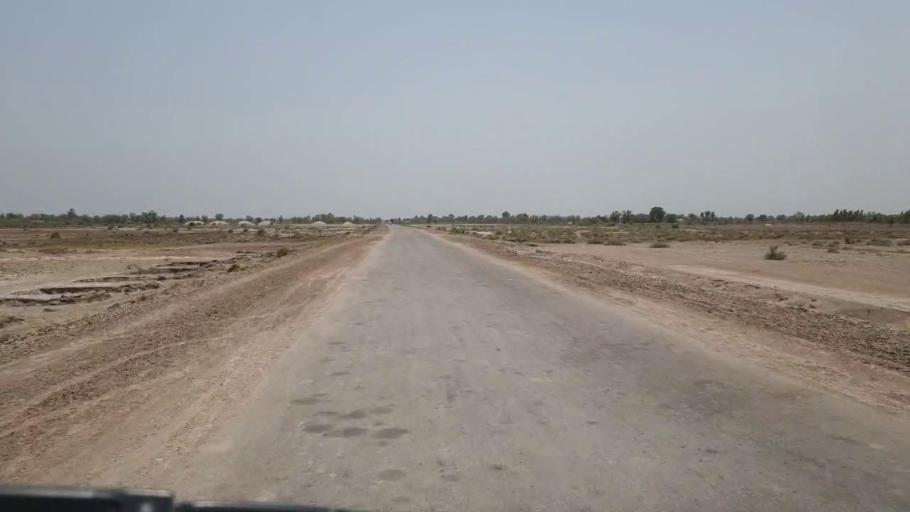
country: PK
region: Sindh
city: Daulatpur
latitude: 26.4540
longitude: 68.1179
